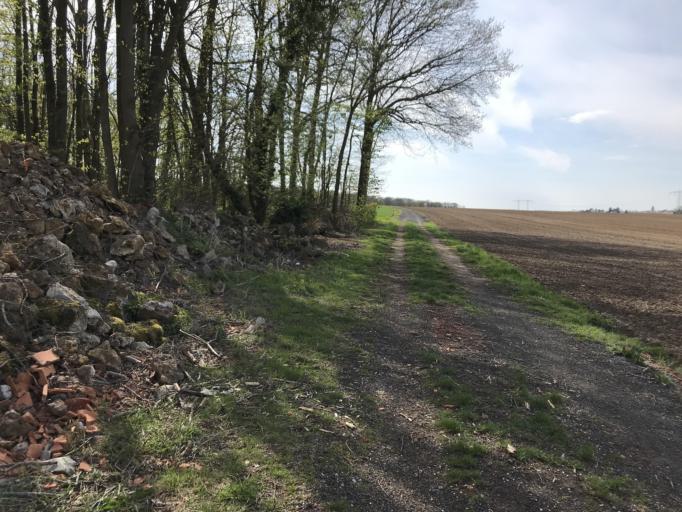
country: FR
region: Ile-de-France
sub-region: Departement de l'Essonne
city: Gometz-le-Chatel
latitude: 48.6679
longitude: 2.1505
